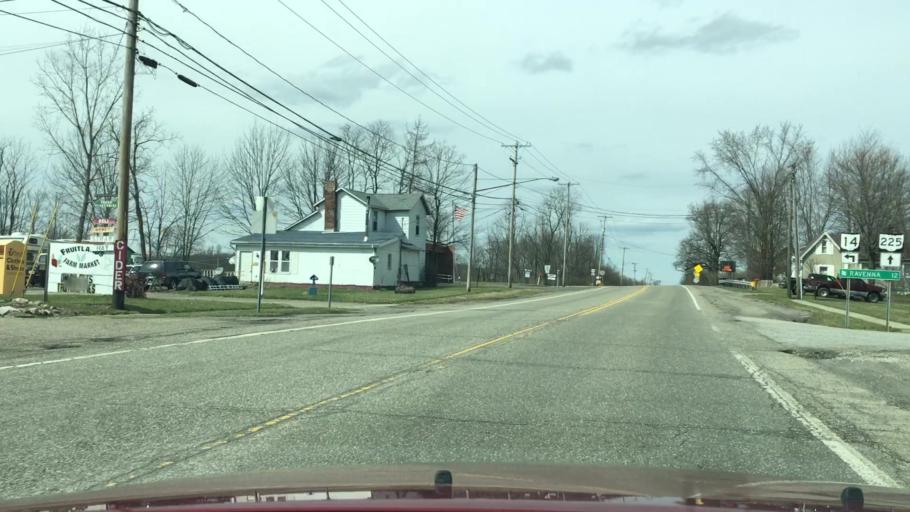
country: US
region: Ohio
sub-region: Mahoning County
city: Sebring
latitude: 41.0254
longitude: -81.0503
